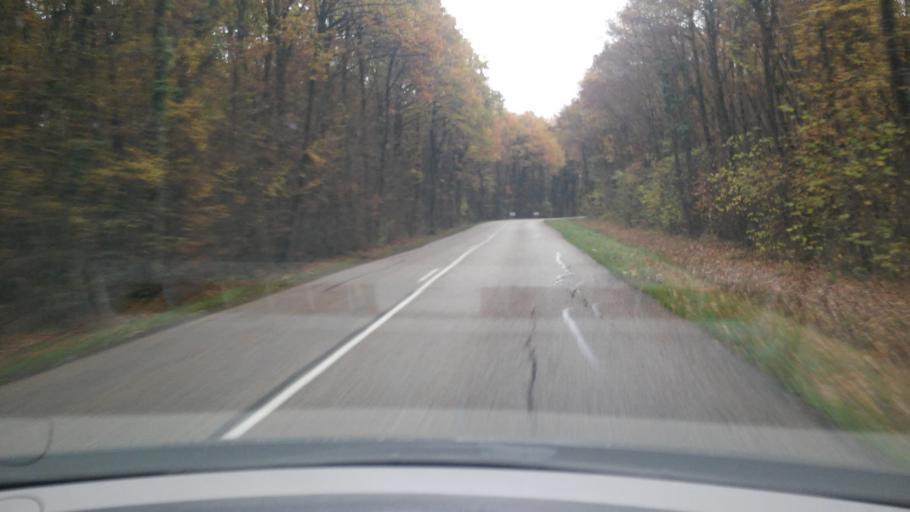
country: FR
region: Lorraine
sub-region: Departement de la Moselle
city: Rurange-les-Thionville
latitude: 49.2787
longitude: 6.2239
